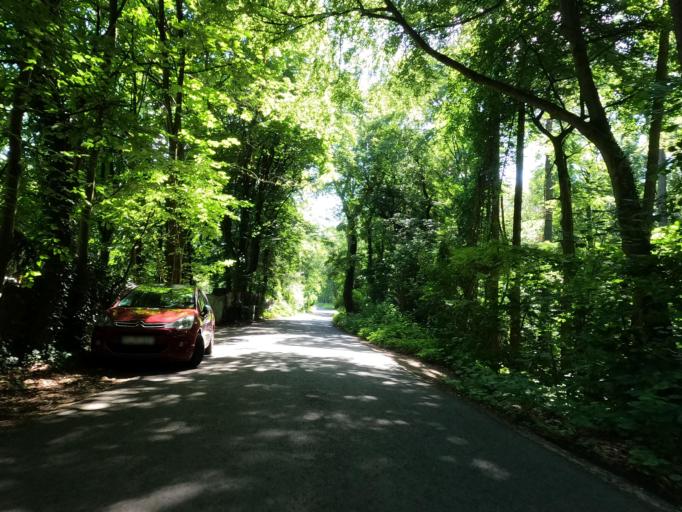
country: DE
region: Hesse
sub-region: Regierungsbezirk Darmstadt
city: Offenbach
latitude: 50.0941
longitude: 8.7291
